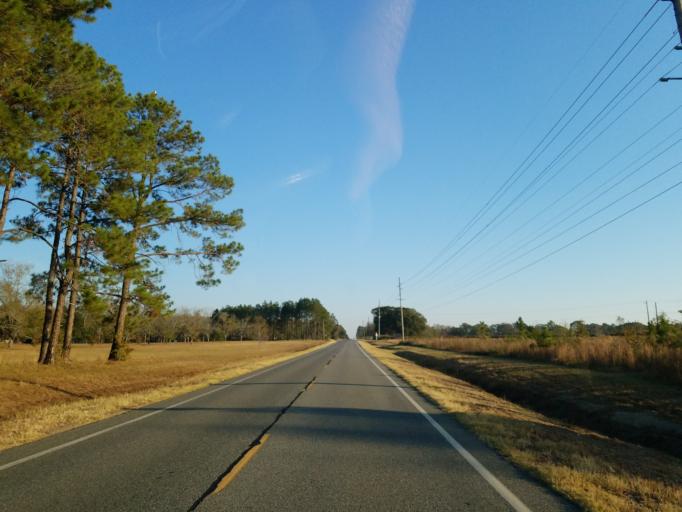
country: US
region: Georgia
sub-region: Crisp County
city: Cordele
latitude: 31.9266
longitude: -83.7222
